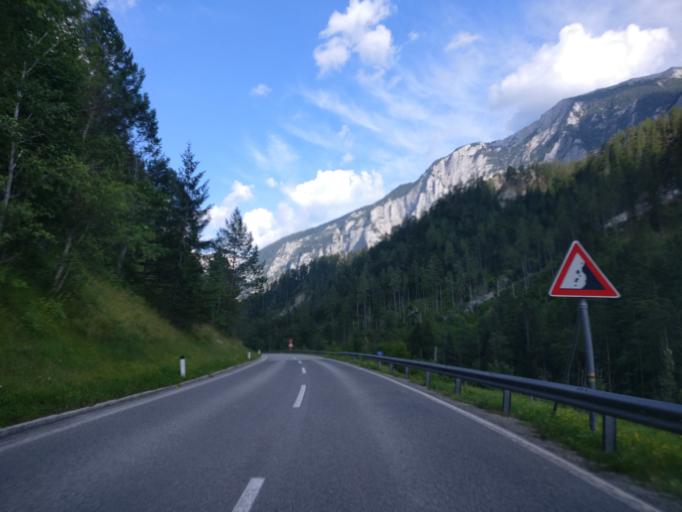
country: AT
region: Styria
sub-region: Politischer Bezirk Liezen
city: Johnsbach
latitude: 47.5904
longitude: 14.6389
